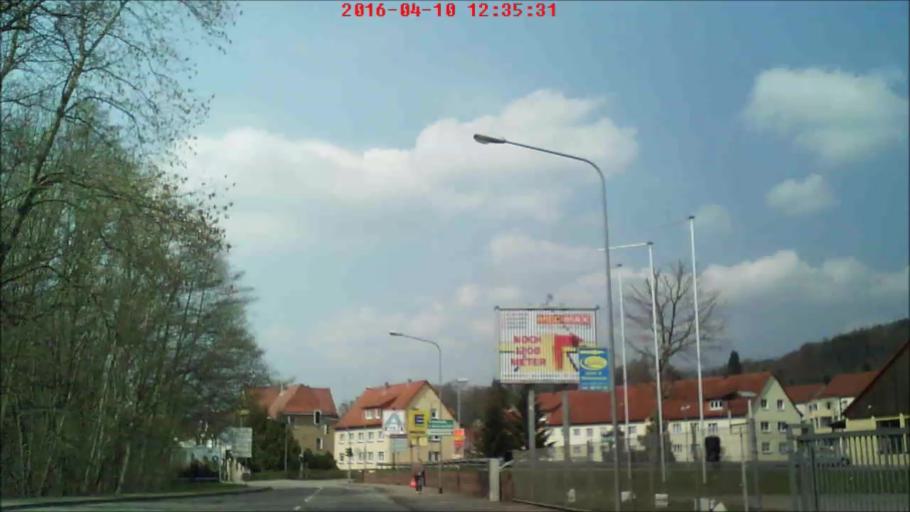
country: DE
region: Thuringia
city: Schmalkalden
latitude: 50.7170
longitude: 10.4672
